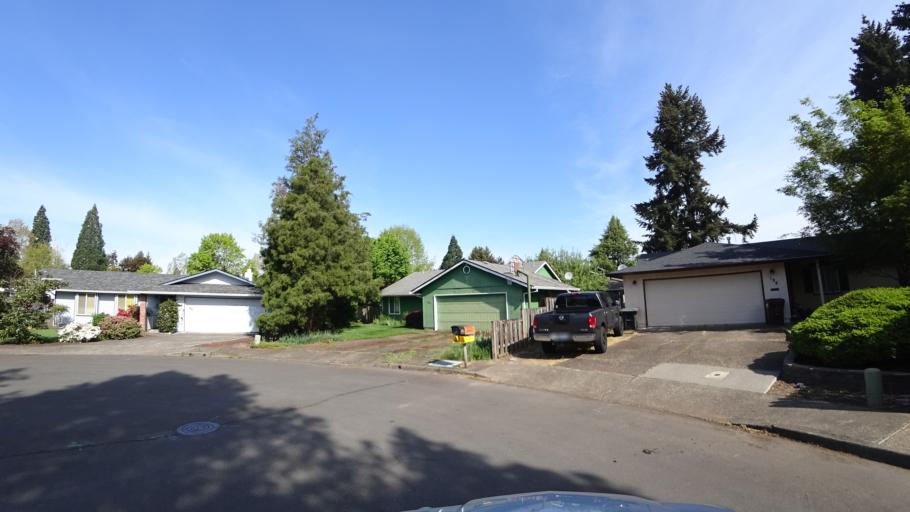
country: US
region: Oregon
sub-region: Washington County
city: Hillsboro
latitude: 45.5218
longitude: -122.9484
